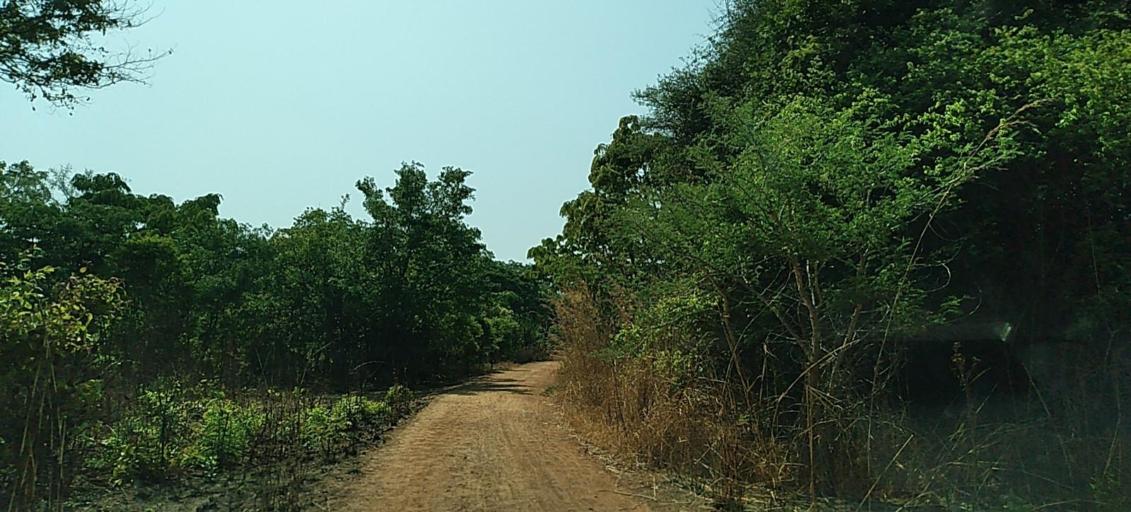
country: ZM
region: Copperbelt
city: Luanshya
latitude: -13.2785
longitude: 28.3093
